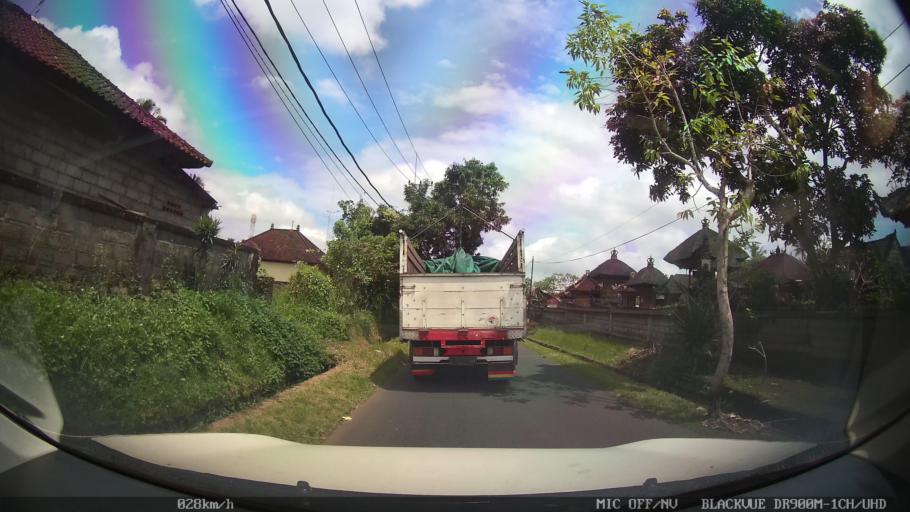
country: ID
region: Bali
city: Banjar Kelodan
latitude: -8.4871
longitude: 115.3676
